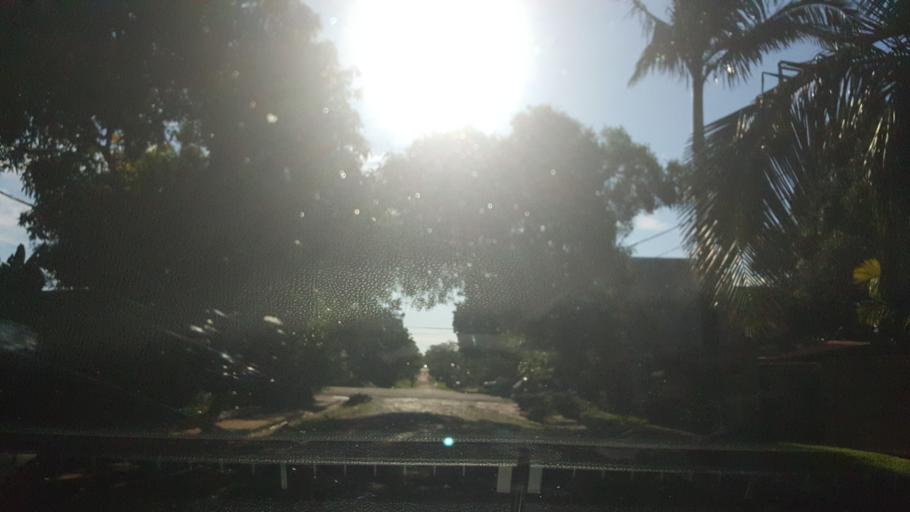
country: AR
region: Misiones
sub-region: Departamento de Capital
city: Posadas
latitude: -27.3808
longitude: -55.9169
